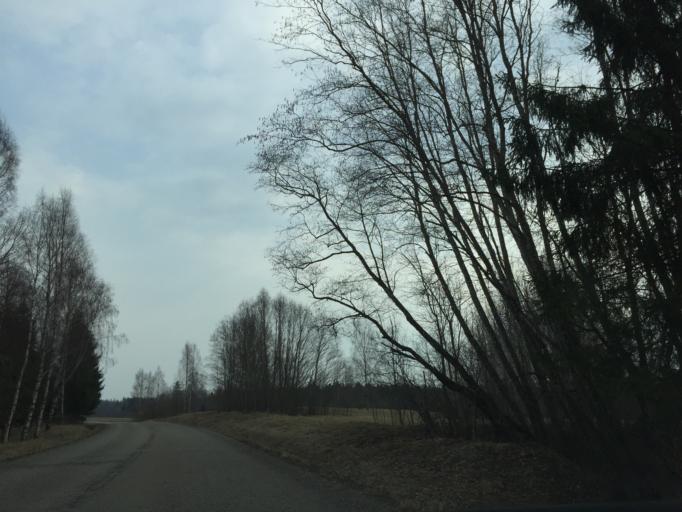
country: LV
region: Priekuli
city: Priekuli
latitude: 57.2195
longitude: 25.3892
